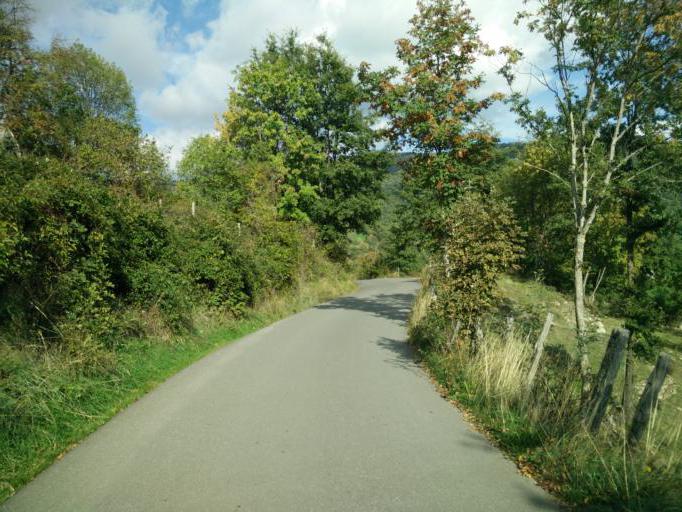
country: IT
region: Tuscany
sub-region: Provincia di Massa-Carrara
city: Patigno
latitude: 44.3549
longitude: 9.7541
